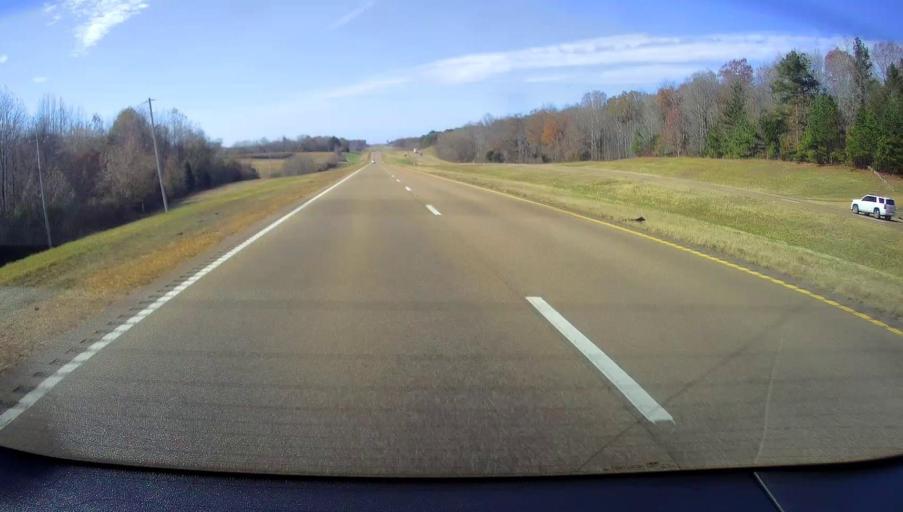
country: US
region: Mississippi
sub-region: Benton County
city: Ashland
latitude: 34.9456
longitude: -89.1516
